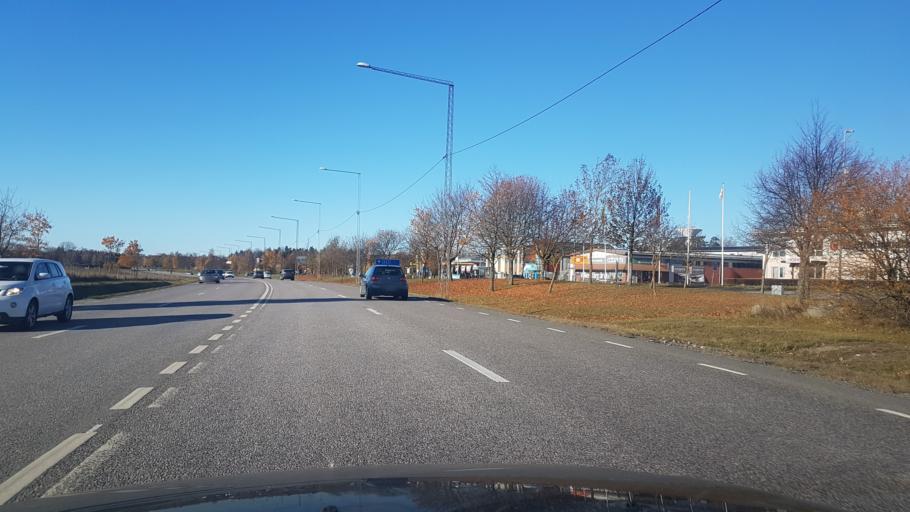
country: SE
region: Stockholm
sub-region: Sigtuna Kommun
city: Marsta
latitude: 59.6129
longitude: 17.8818
